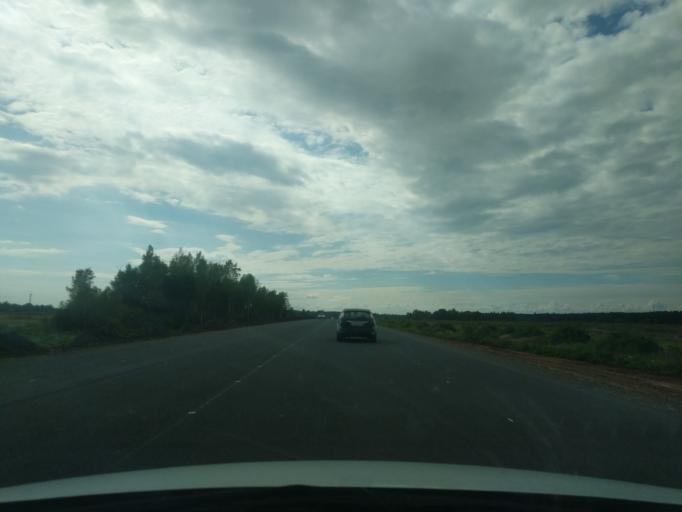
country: RU
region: Kostroma
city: Sudislavl'
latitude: 57.8322
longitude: 41.5467
